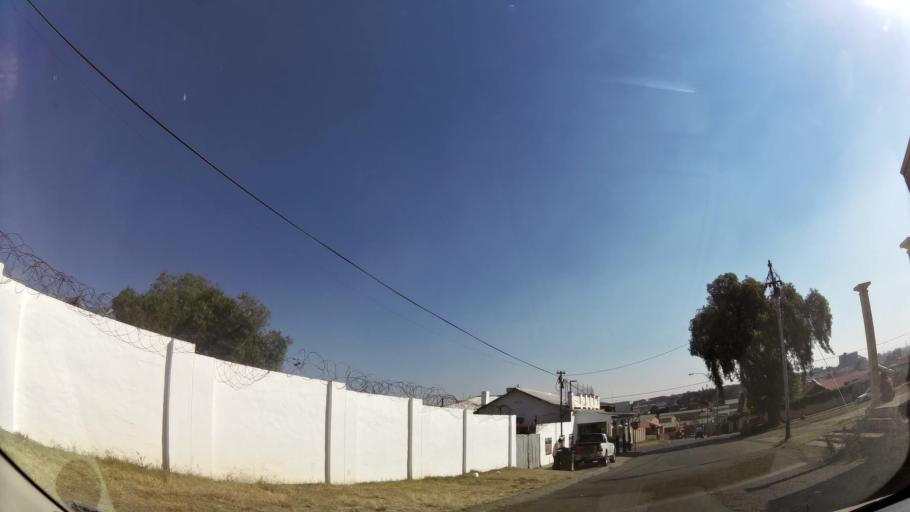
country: ZA
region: Gauteng
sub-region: City of Johannesburg Metropolitan Municipality
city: Johannesburg
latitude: -26.1901
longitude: 27.9665
